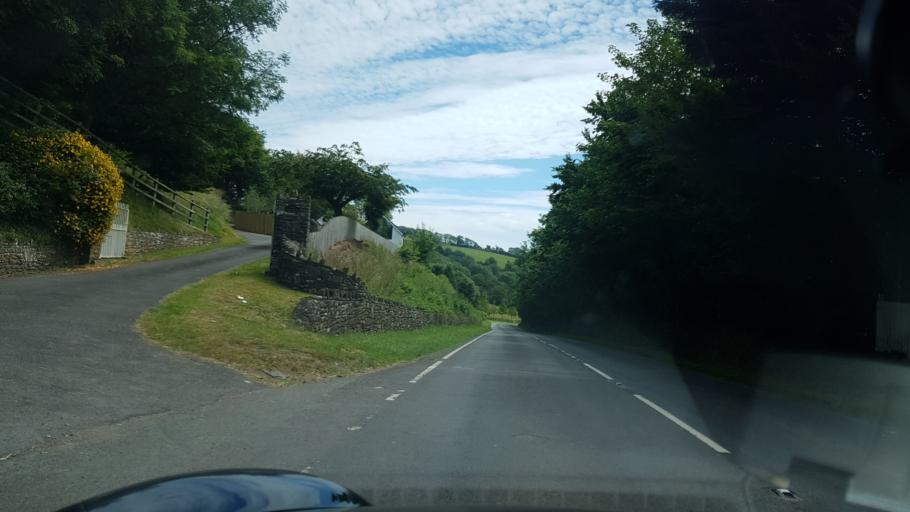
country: GB
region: Wales
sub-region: Carmarthenshire
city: Saint Clears
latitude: 51.7776
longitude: -4.4680
